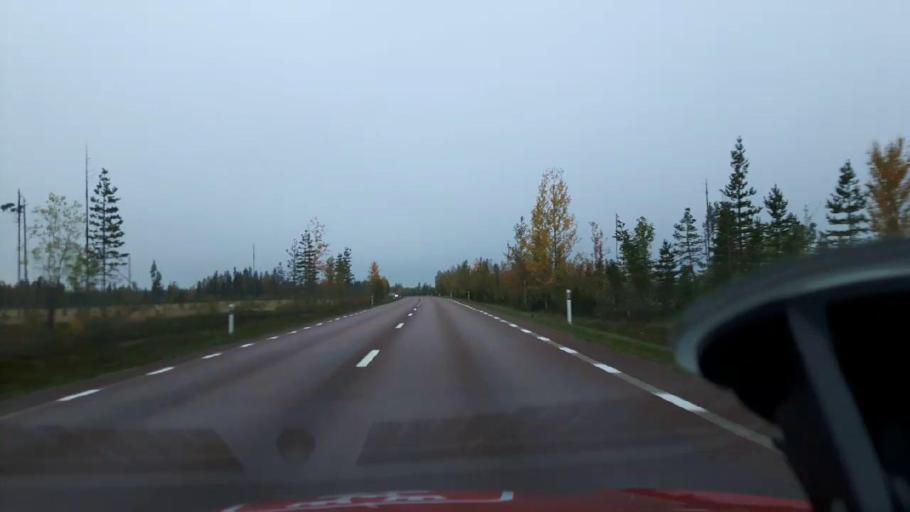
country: SE
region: Jaemtland
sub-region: Bergs Kommun
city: Hoverberg
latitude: 62.5302
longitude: 14.4469
